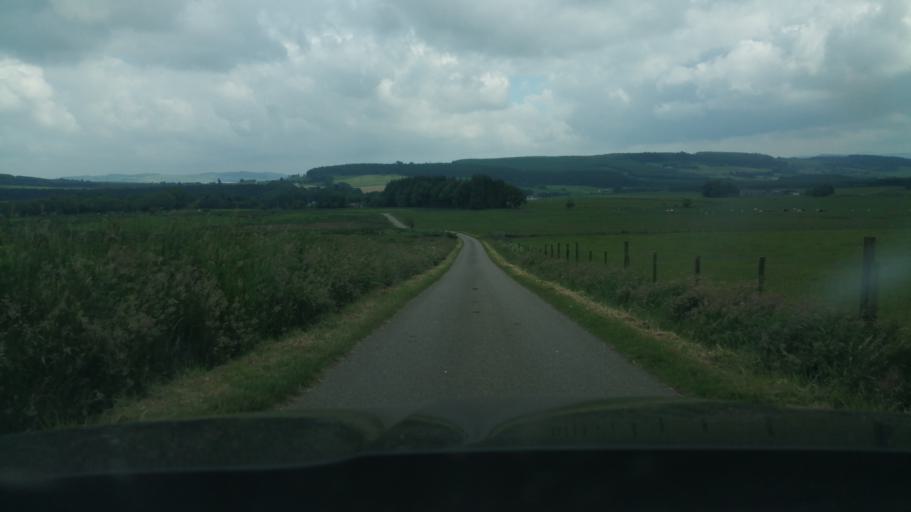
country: GB
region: Scotland
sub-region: Moray
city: Cullen
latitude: 57.5930
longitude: -2.8236
